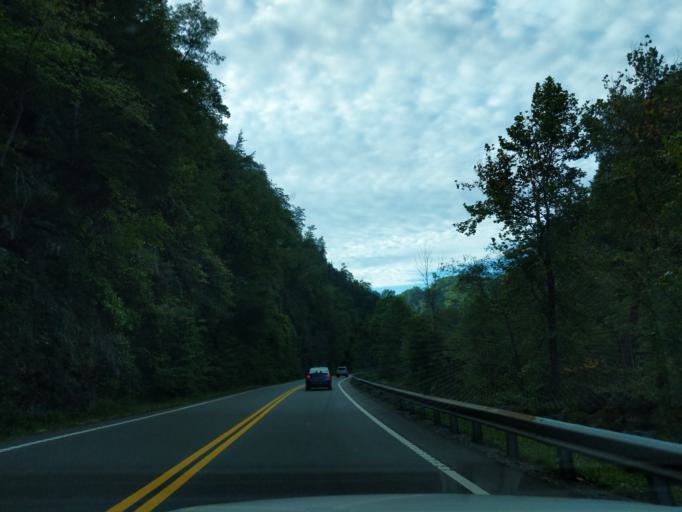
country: US
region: Tennessee
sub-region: Polk County
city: Benton
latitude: 35.0976
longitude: -84.5353
